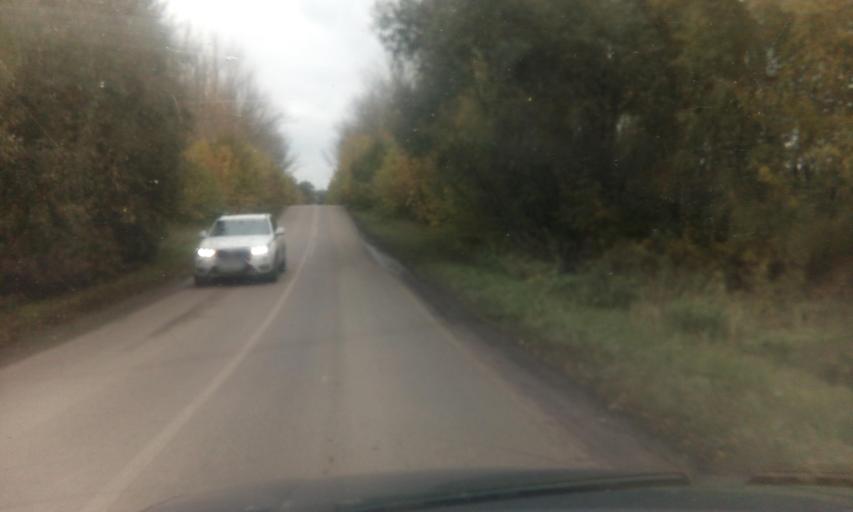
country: RU
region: Tula
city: Uzlovaya
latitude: 53.9734
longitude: 38.1445
